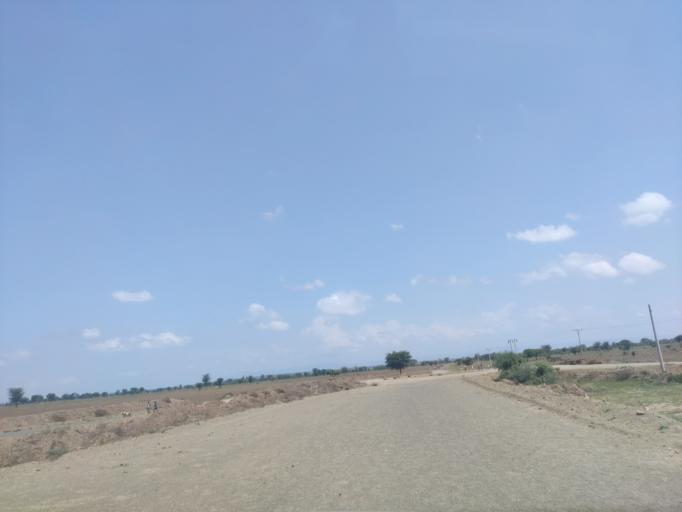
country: ET
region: Oromiya
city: Mojo
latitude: 8.3028
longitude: 38.9330
